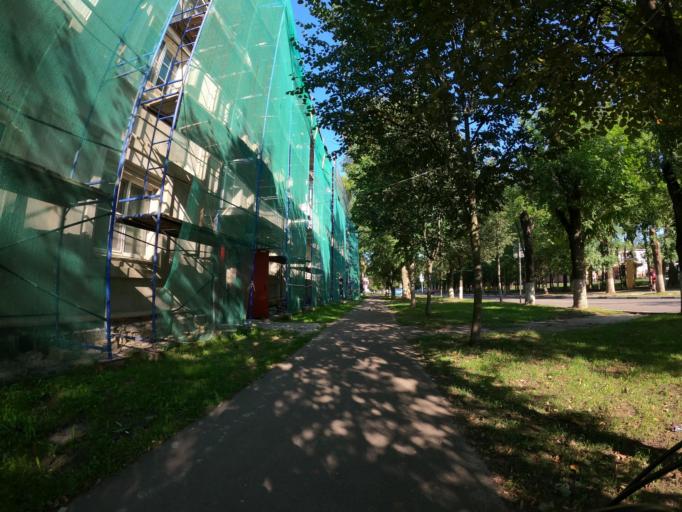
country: RU
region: Moskovskaya
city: Stupino
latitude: 54.8835
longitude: 38.0814
